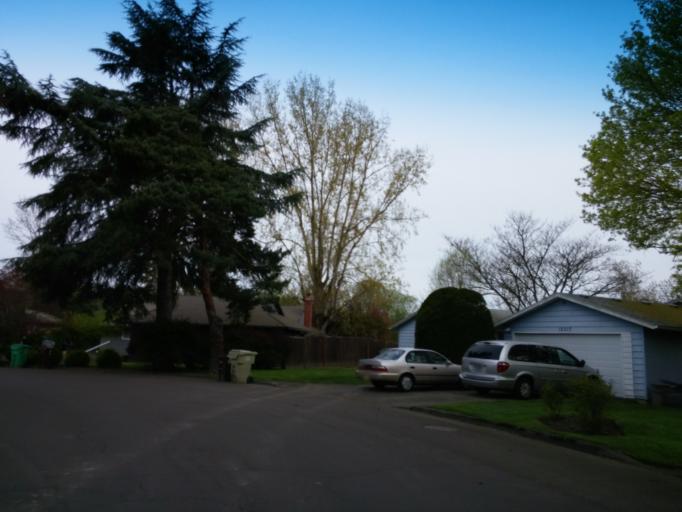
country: US
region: Oregon
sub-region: Washington County
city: Cedar Mill
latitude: 45.5103
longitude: -122.8136
